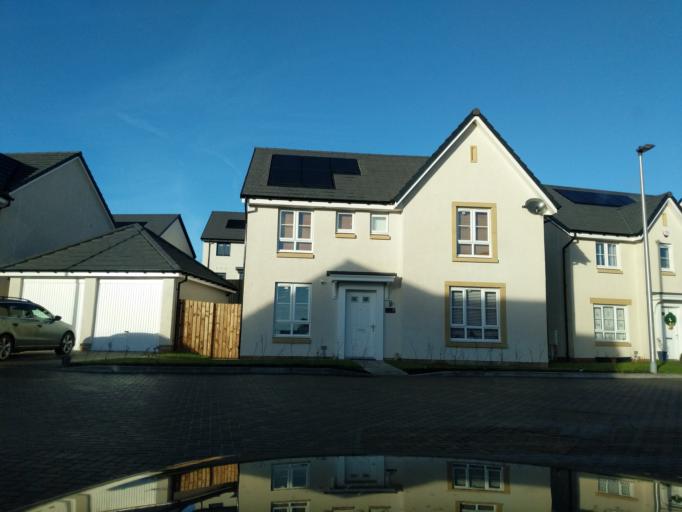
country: GB
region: Scotland
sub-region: Midlothian
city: Loanhead
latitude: 55.8962
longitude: -3.1650
